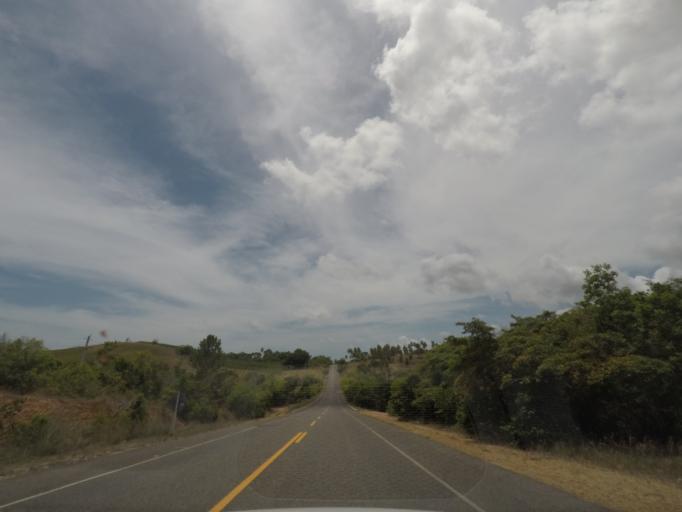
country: BR
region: Bahia
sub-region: Conde
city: Conde
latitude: -11.8829
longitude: -37.6493
